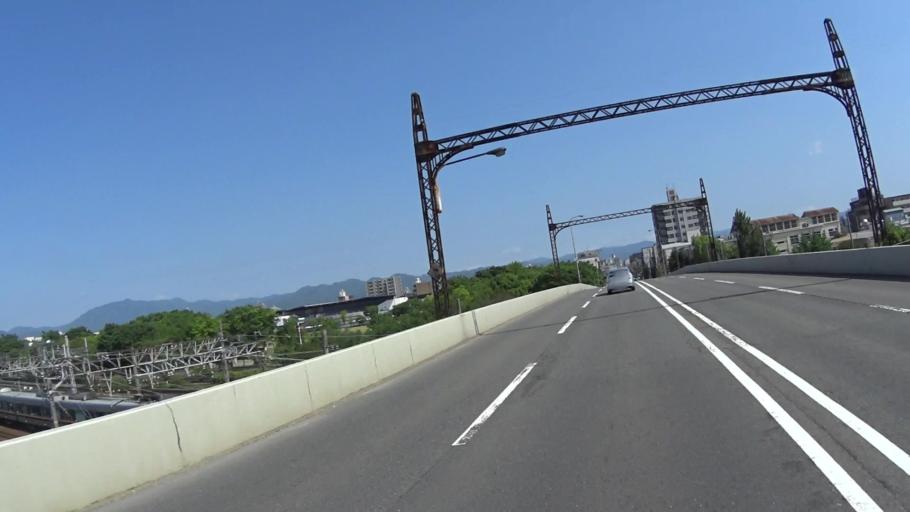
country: JP
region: Kyoto
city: Kyoto
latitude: 34.9849
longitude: 135.7492
